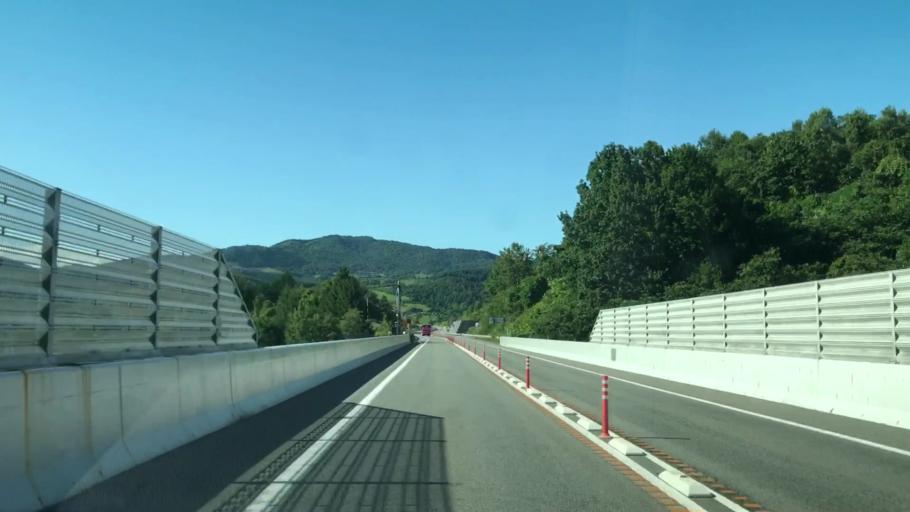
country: JP
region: Hokkaido
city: Date
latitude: 42.5392
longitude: 140.7967
